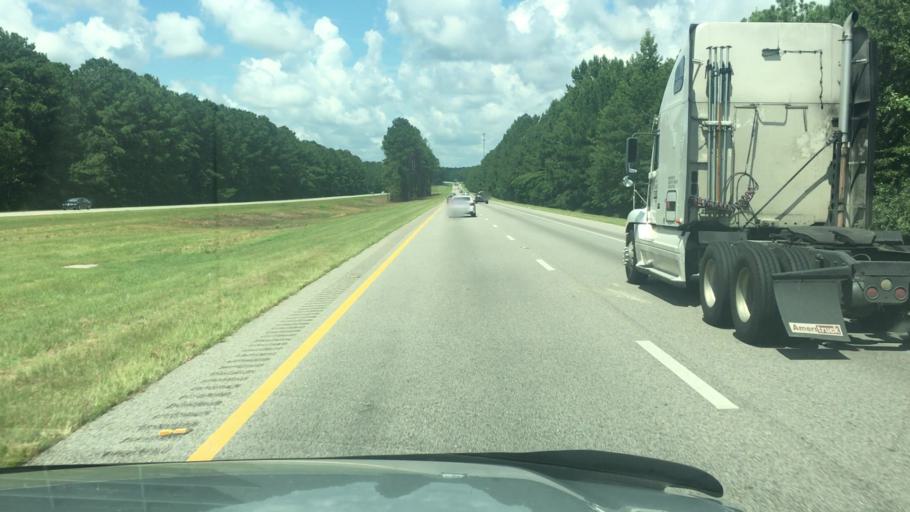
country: US
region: South Carolina
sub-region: Kershaw County
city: Camden
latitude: 34.2118
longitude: -80.4918
